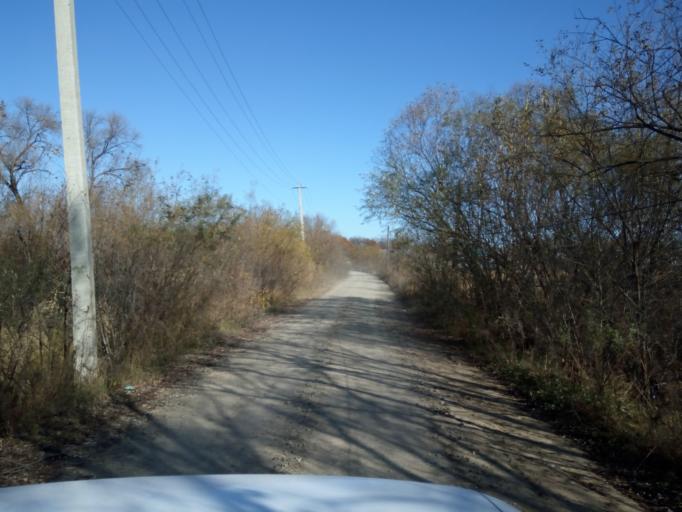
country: RU
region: Primorskiy
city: Dal'nerechensk
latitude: 45.9135
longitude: 133.8050
